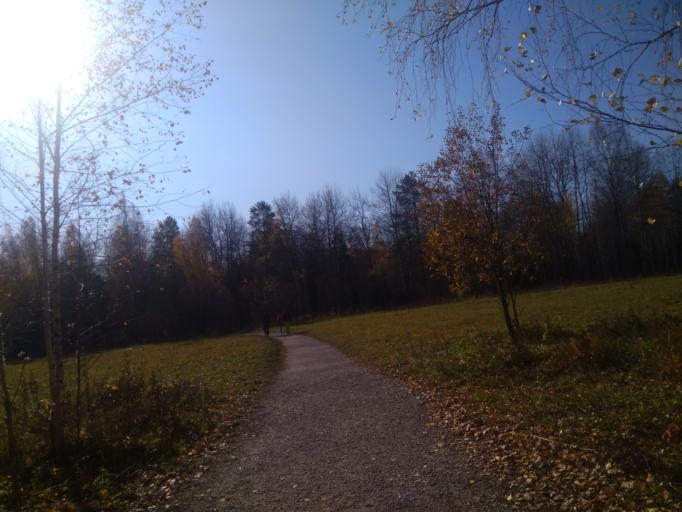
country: RU
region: Sverdlovsk
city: Mikhaylovsk
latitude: 56.5223
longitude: 59.2350
